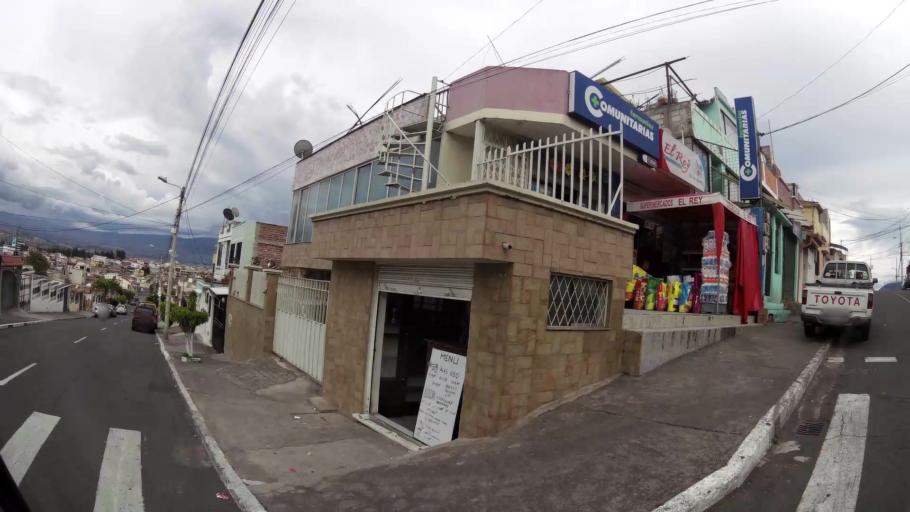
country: EC
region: Tungurahua
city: Ambato
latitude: -1.2610
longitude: -78.6328
